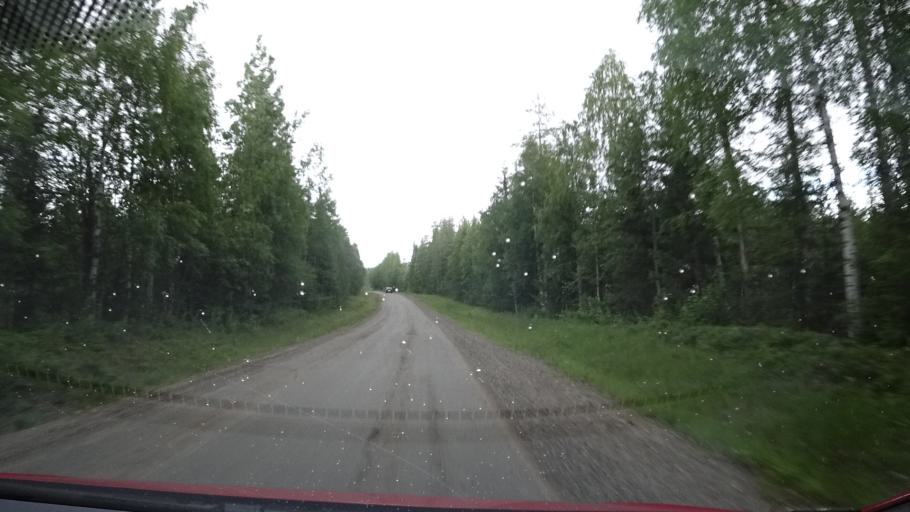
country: FI
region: Kainuu
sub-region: Kehys-Kainuu
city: Kuhmo
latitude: 63.9419
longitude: 29.2124
